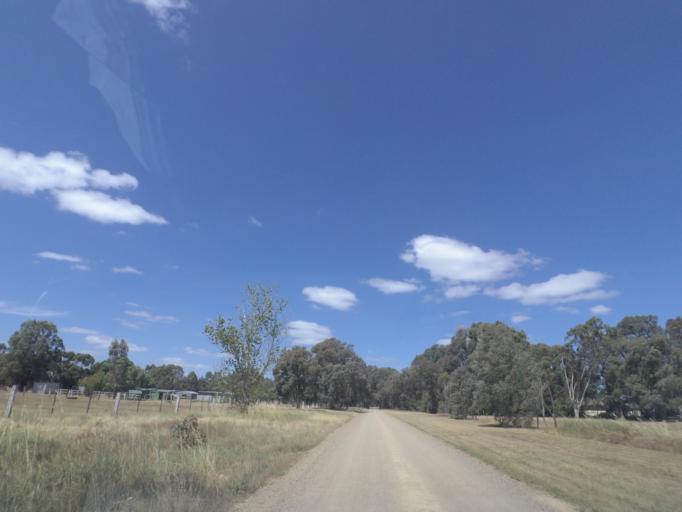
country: AU
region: Victoria
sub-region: Wangaratta
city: Wangaratta
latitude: -36.3990
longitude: 146.2851
